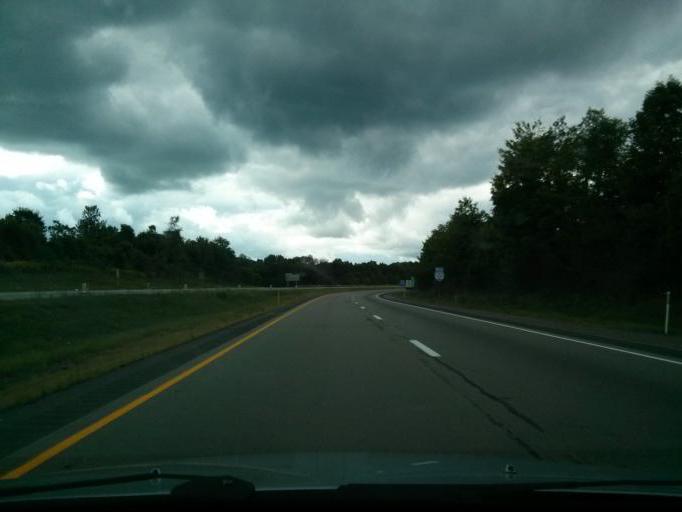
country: US
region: Pennsylvania
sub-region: Clarion County
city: Clarion
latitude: 41.1811
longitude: -79.2456
